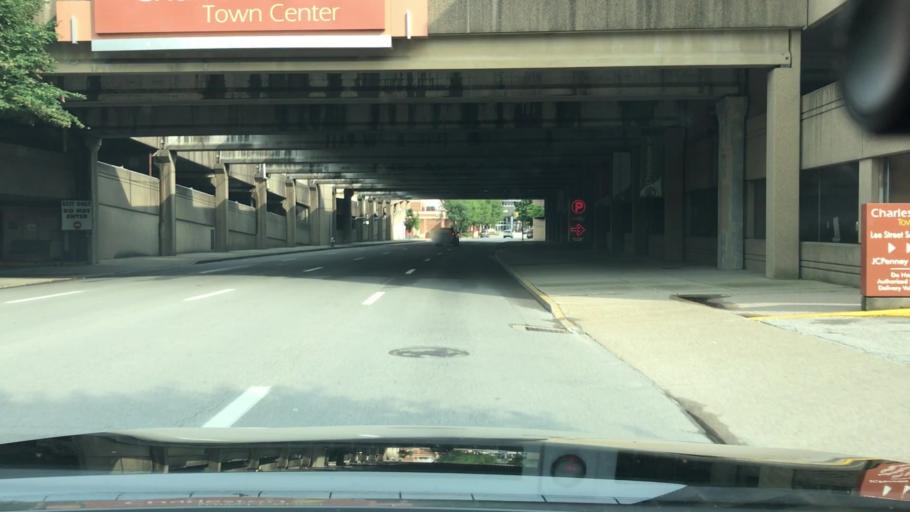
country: US
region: West Virginia
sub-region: Kanawha County
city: Charleston
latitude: 38.3552
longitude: -81.6376
